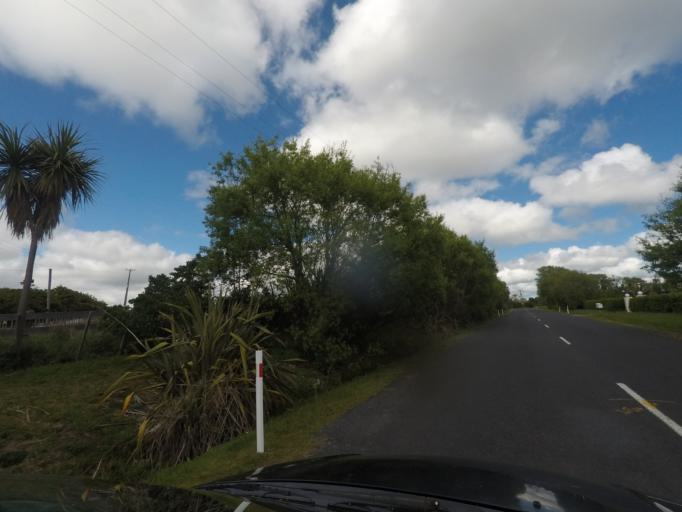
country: NZ
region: Auckland
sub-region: Auckland
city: Rothesay Bay
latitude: -36.7643
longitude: 174.6455
